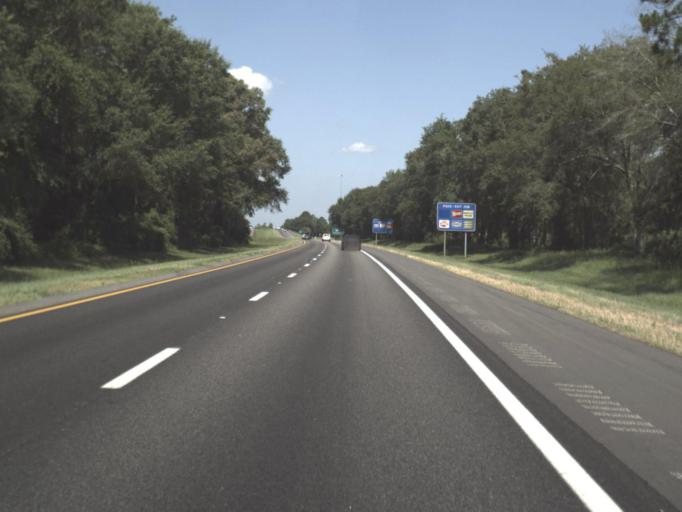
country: US
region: Florida
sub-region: Madison County
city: Madison
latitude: 30.3941
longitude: -83.3461
